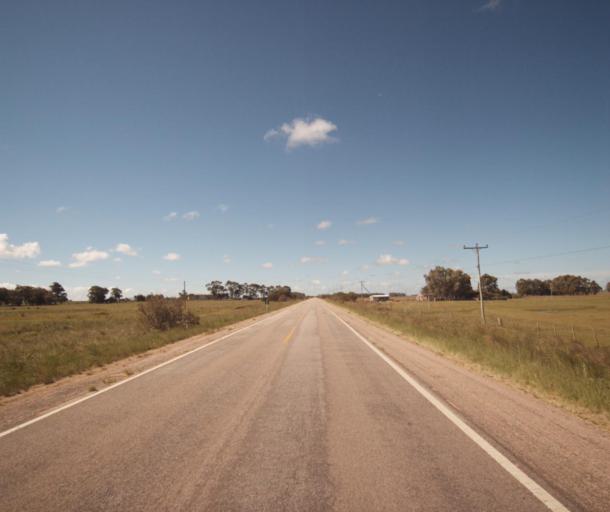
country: BR
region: Rio Grande do Sul
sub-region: Chui
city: Chui
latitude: -33.6382
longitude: -53.4202
